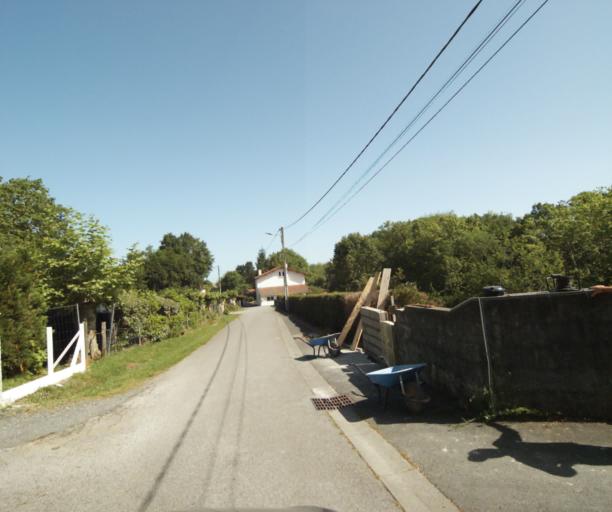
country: FR
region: Aquitaine
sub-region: Departement des Pyrenees-Atlantiques
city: Villefranque
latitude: 43.4599
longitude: -1.4446
